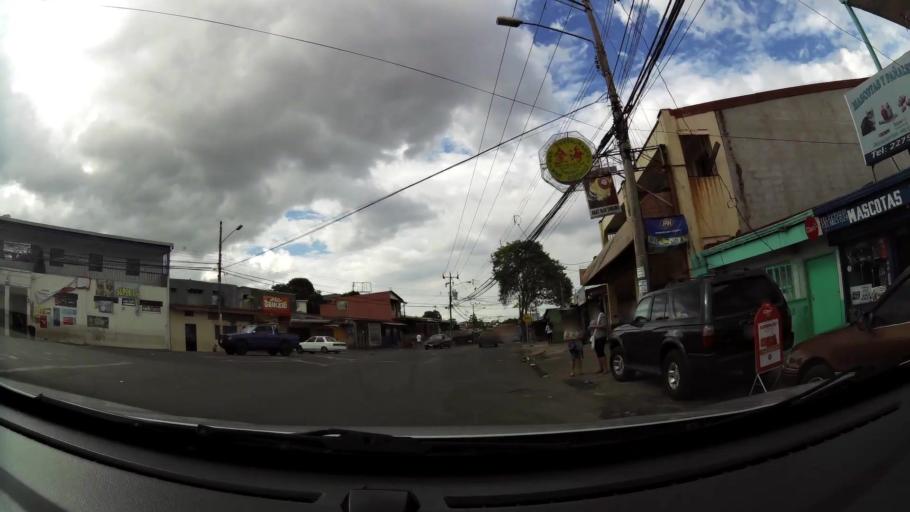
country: CR
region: San Jose
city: Alajuelita
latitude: 9.8978
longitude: -84.0924
